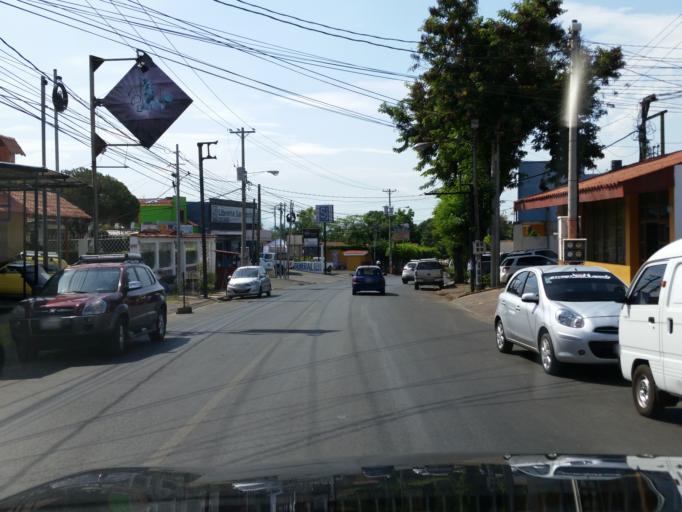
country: NI
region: Managua
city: Managua
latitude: 12.1248
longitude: -86.2617
